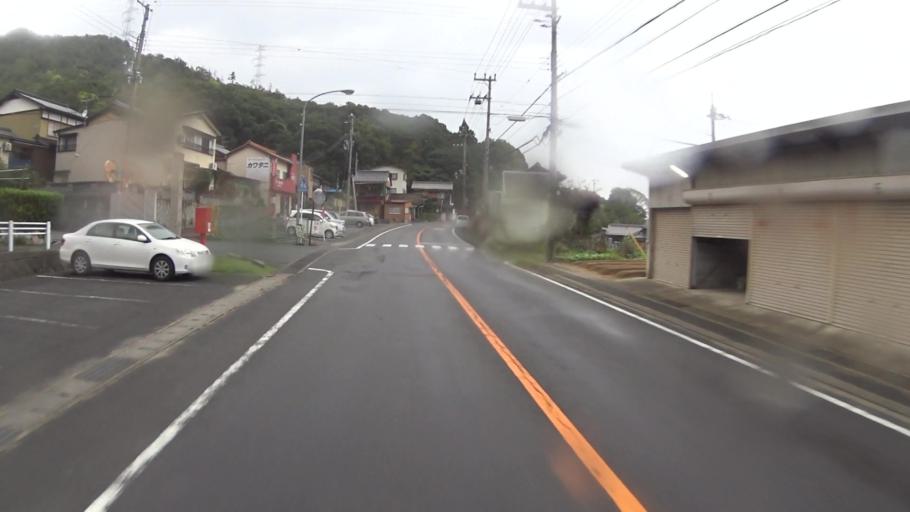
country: JP
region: Kyoto
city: Miyazu
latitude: 35.5550
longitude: 135.2359
